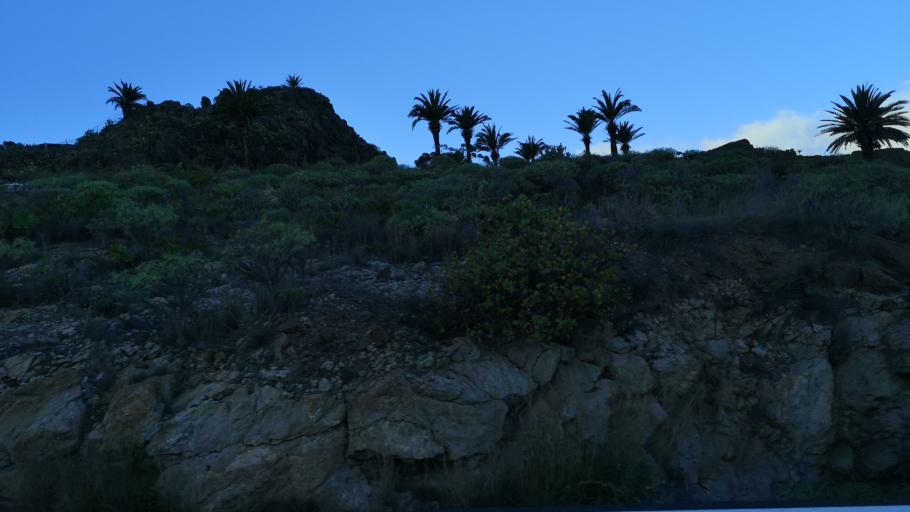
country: ES
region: Canary Islands
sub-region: Provincia de Santa Cruz de Tenerife
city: Alajero
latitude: 28.0570
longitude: -17.2297
